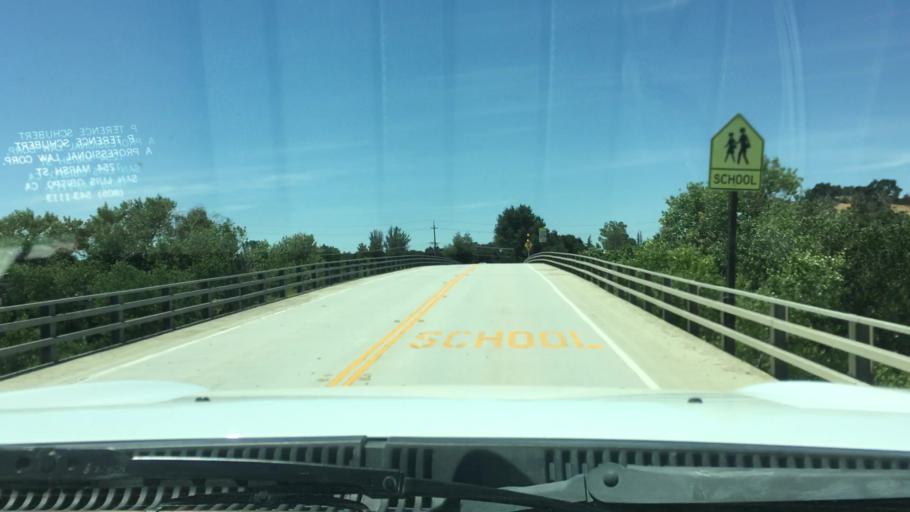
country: US
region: California
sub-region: San Luis Obispo County
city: Templeton
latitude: 35.5432
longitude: -120.7069
